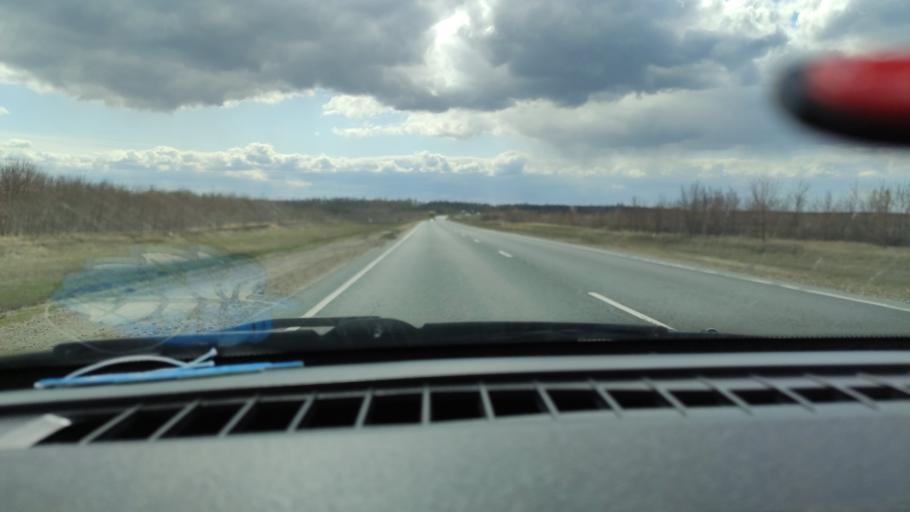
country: RU
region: Saratov
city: Alekseyevka
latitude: 52.2801
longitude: 47.9318
